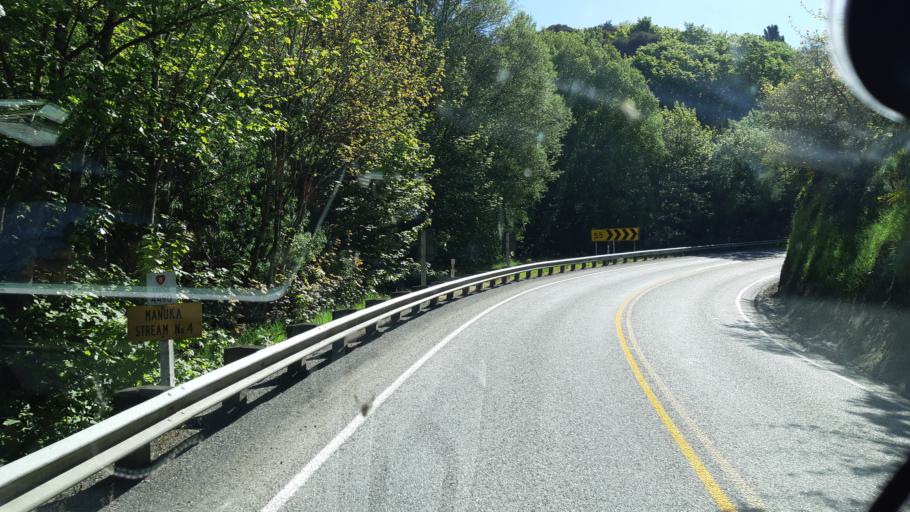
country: NZ
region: Otago
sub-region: Clutha District
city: Milton
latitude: -46.0694
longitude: 169.8301
